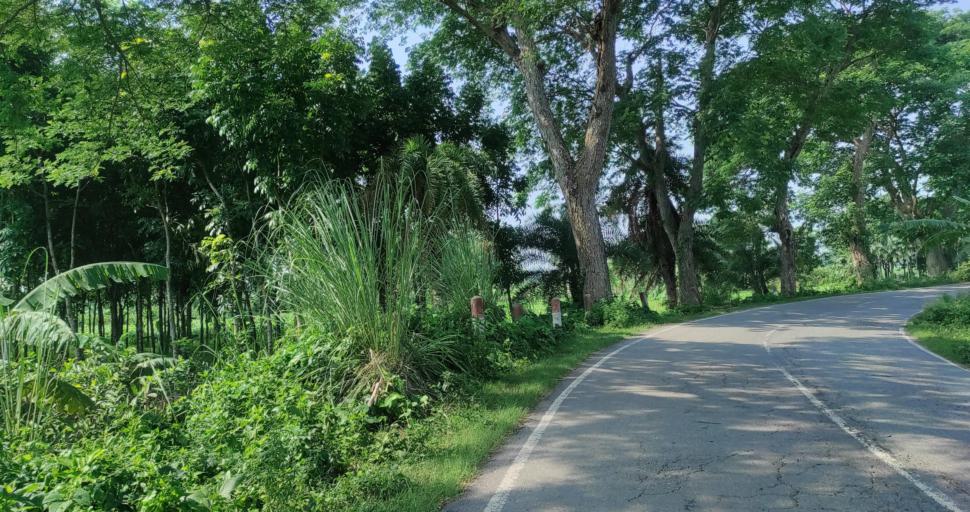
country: BD
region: Rajshahi
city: Ishurdi
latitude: 24.2798
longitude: 89.0642
